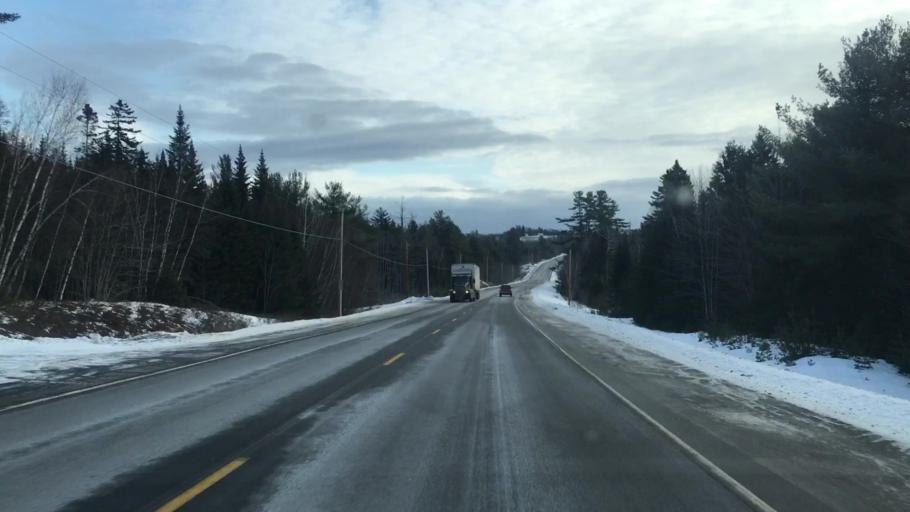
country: US
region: Maine
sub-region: Washington County
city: Machias
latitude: 44.9501
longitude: -67.6844
